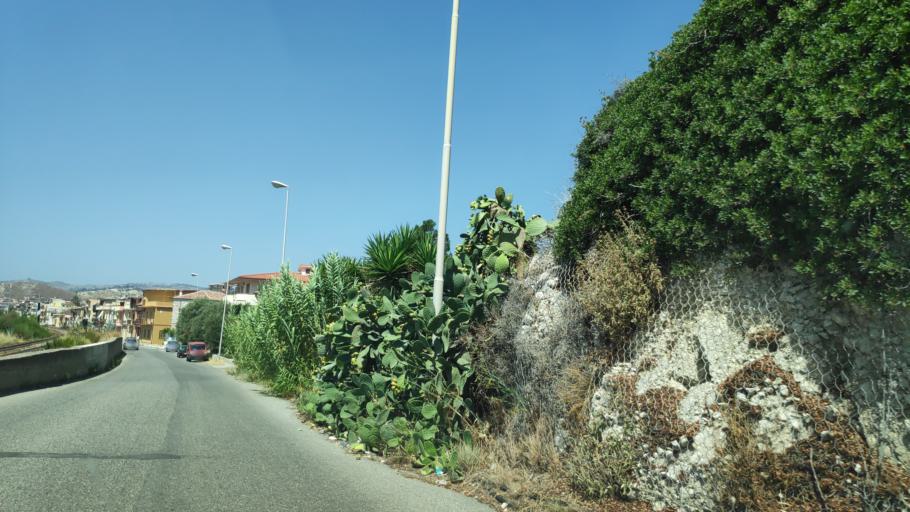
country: IT
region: Calabria
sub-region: Provincia di Reggio Calabria
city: Bova Marina
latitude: 37.9289
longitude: 15.9320
